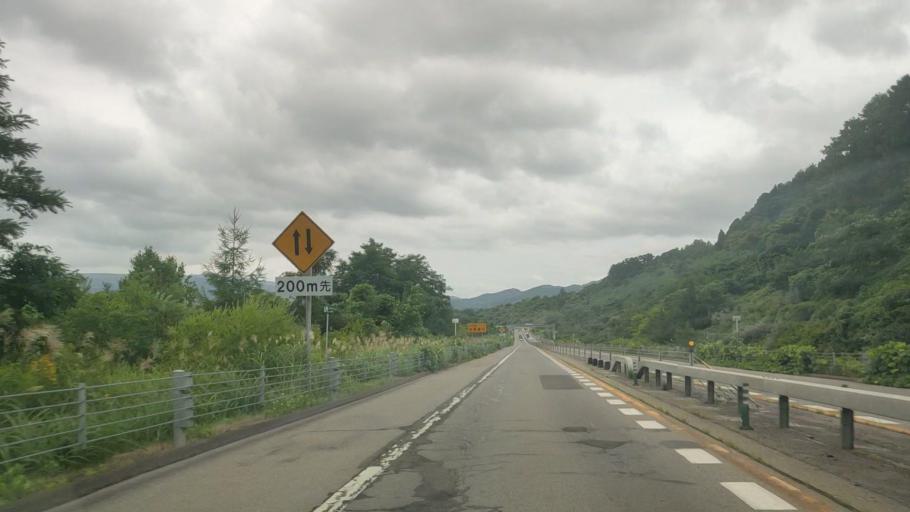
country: JP
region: Hokkaido
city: Nanae
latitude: 41.9093
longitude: 140.6946
